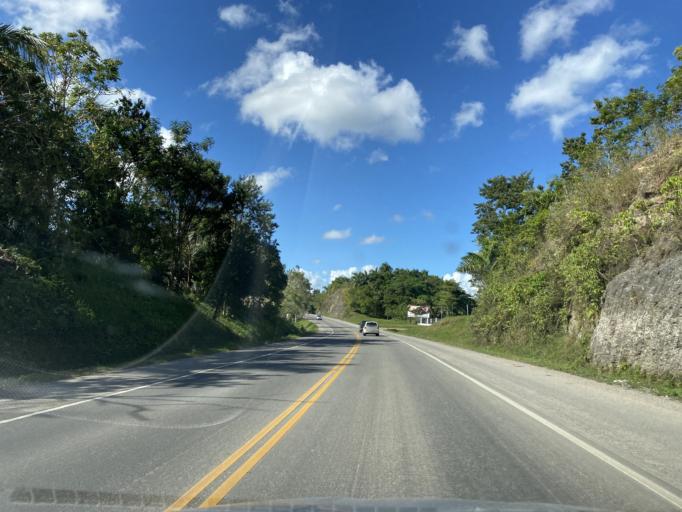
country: DO
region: Monte Plata
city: Gonzalo
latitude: 18.9634
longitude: -69.7644
